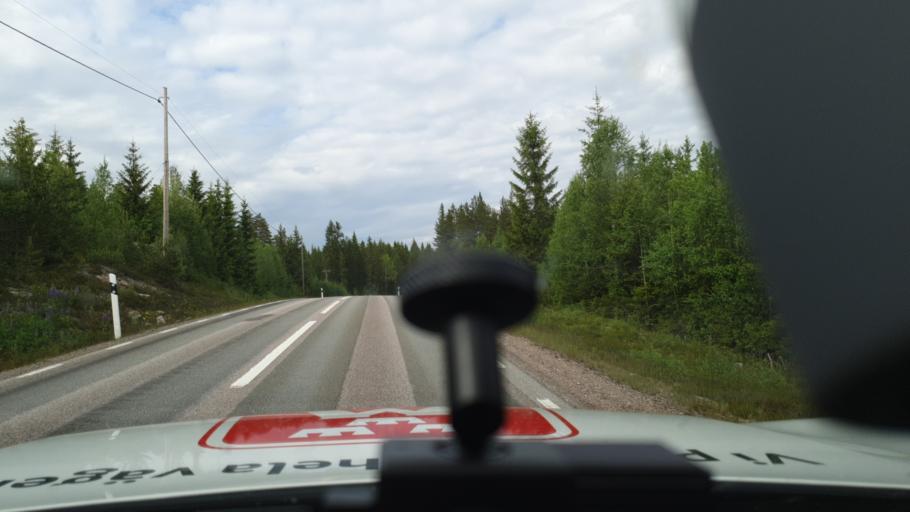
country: SE
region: Vaermland
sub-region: Torsby Kommun
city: Torsby
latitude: 60.3127
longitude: 13.0981
